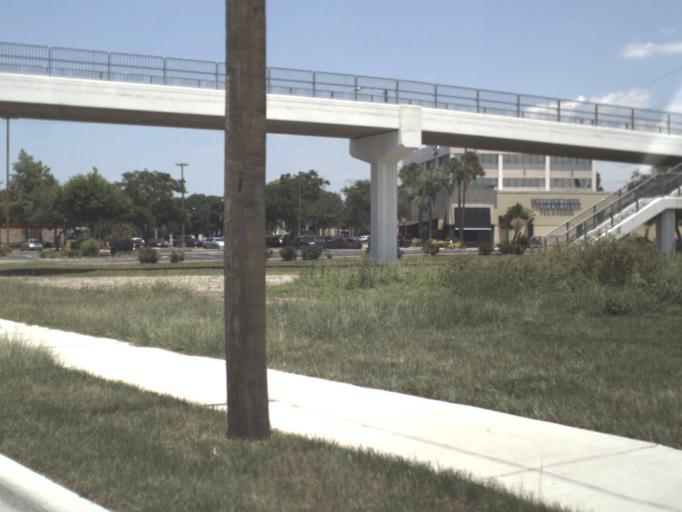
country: US
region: Florida
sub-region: Pinellas County
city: Safety Harbor
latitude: 28.0086
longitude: -82.7304
